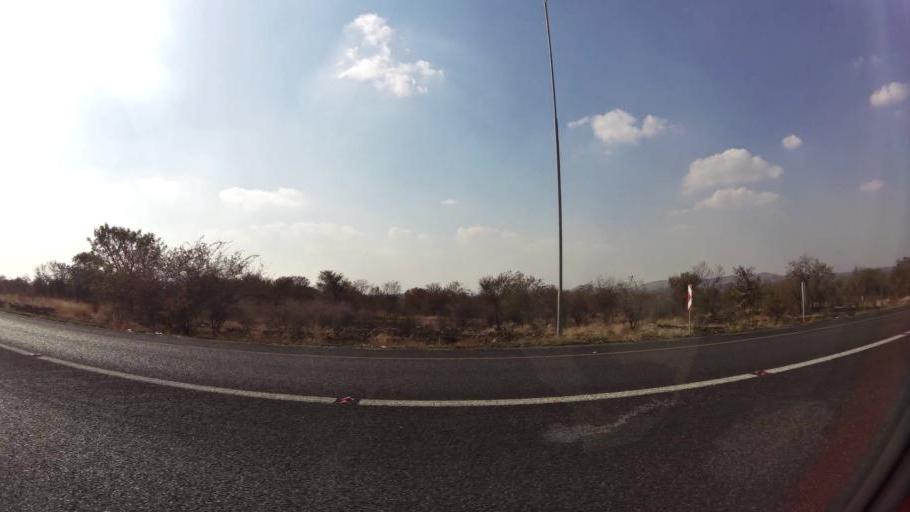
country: ZA
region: North-West
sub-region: Bojanala Platinum District Municipality
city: Rustenburg
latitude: -25.6027
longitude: 27.1365
